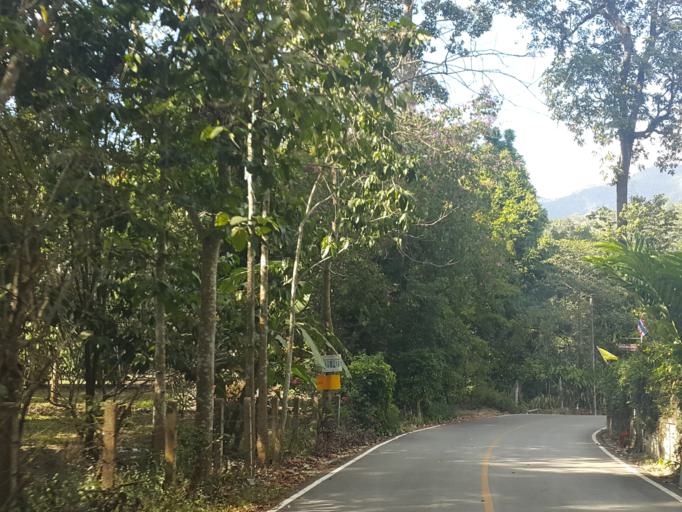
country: TH
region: Chiang Mai
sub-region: Amphoe Chiang Dao
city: Chiang Dao
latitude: 19.4022
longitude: 98.9282
